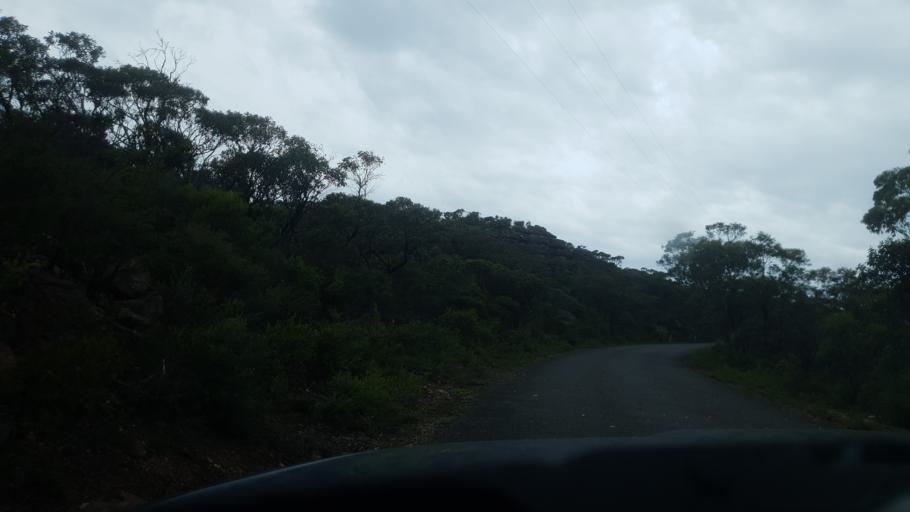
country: AU
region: Victoria
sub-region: Northern Grampians
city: Stawell
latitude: -37.2809
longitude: 142.5862
